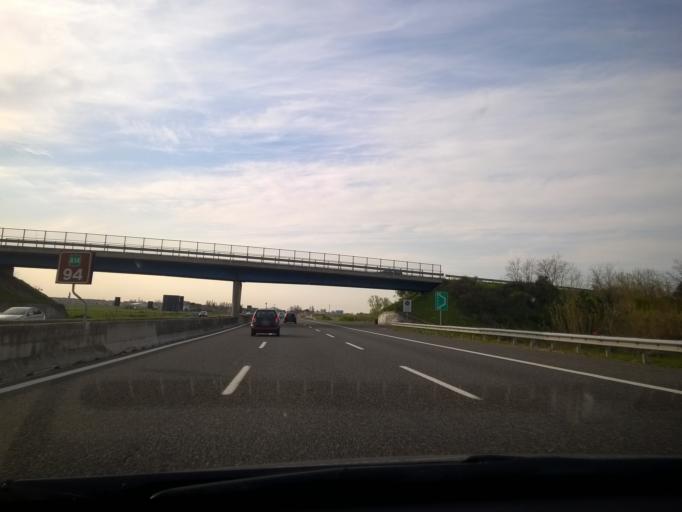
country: IT
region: Emilia-Romagna
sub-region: Forli-Cesena
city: San Mauro Pascoli
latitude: 44.1031
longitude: 12.4369
